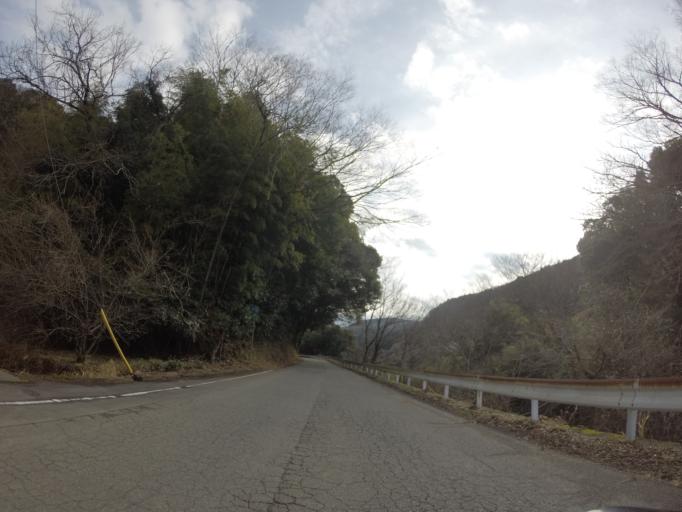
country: JP
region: Shizuoka
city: Heda
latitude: 34.8913
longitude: 138.8914
